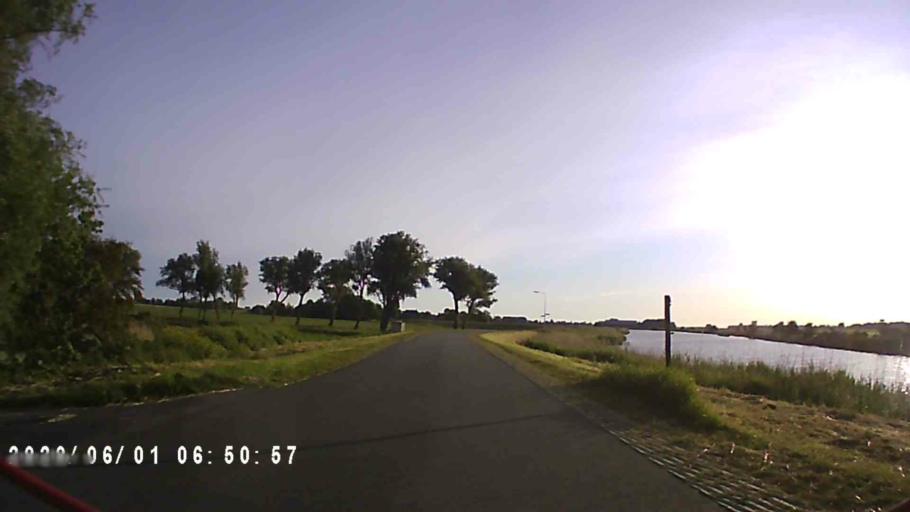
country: NL
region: Friesland
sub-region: Gemeente Kollumerland en Nieuwkruisland
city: Kollum
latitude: 53.3038
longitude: 6.1306
